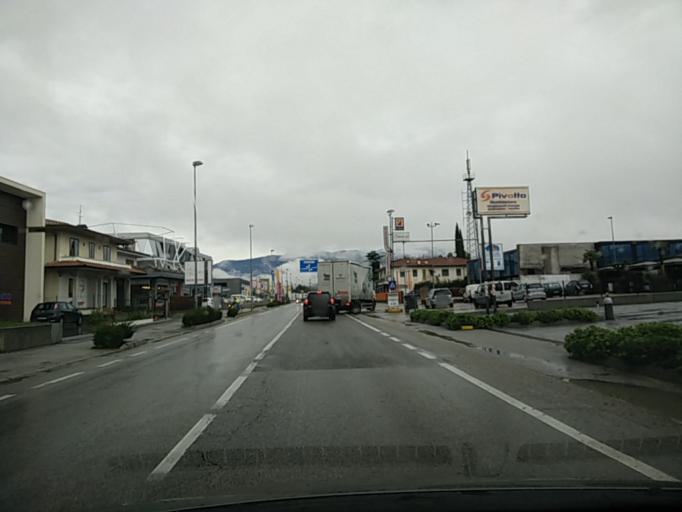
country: IT
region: Veneto
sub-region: Provincia di Vicenza
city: San Zeno-San Giuseppe
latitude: 45.7325
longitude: 11.7607
